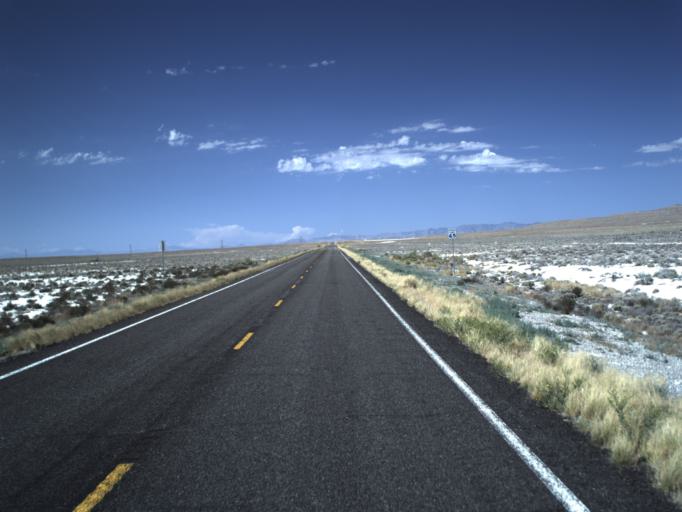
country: US
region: Utah
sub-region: Millard County
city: Delta
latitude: 39.1866
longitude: -113.0070
